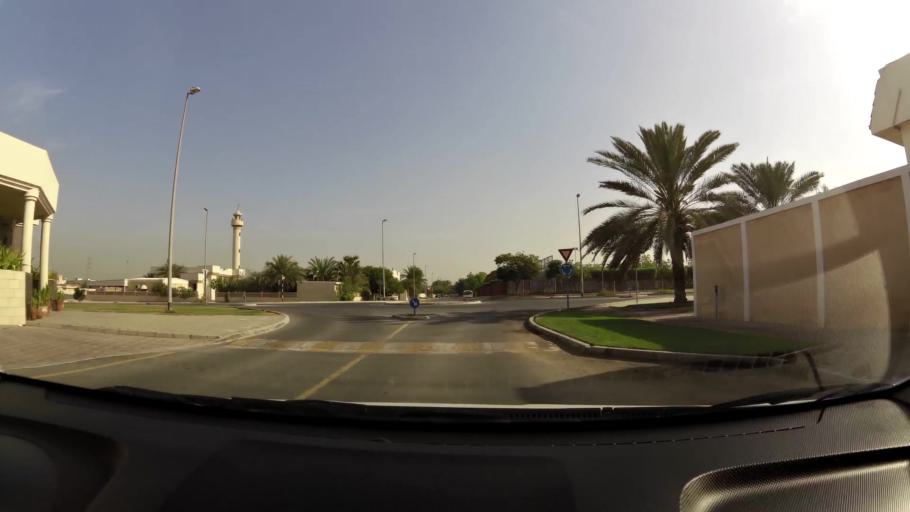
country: AE
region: Ash Shariqah
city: Sharjah
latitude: 25.2469
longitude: 55.4109
